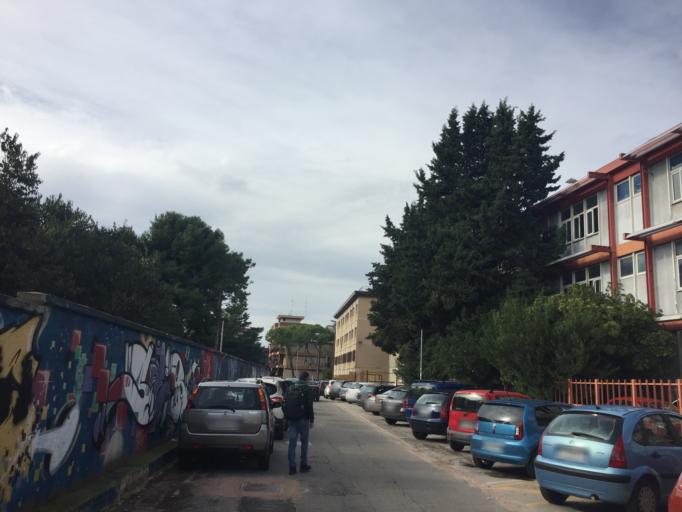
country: IT
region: Apulia
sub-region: Provincia di Bari
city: Bari
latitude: 41.1105
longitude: 16.8783
